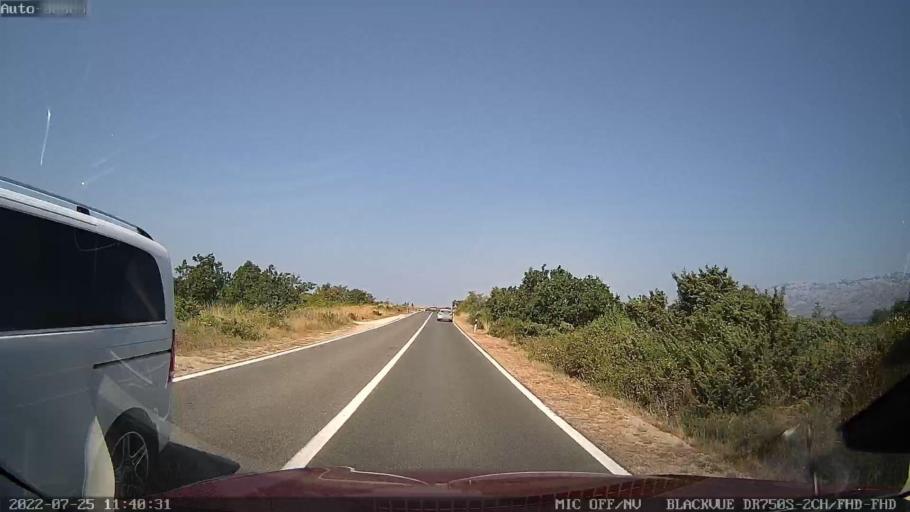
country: HR
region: Zadarska
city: Razanac
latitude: 44.2637
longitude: 15.3590
